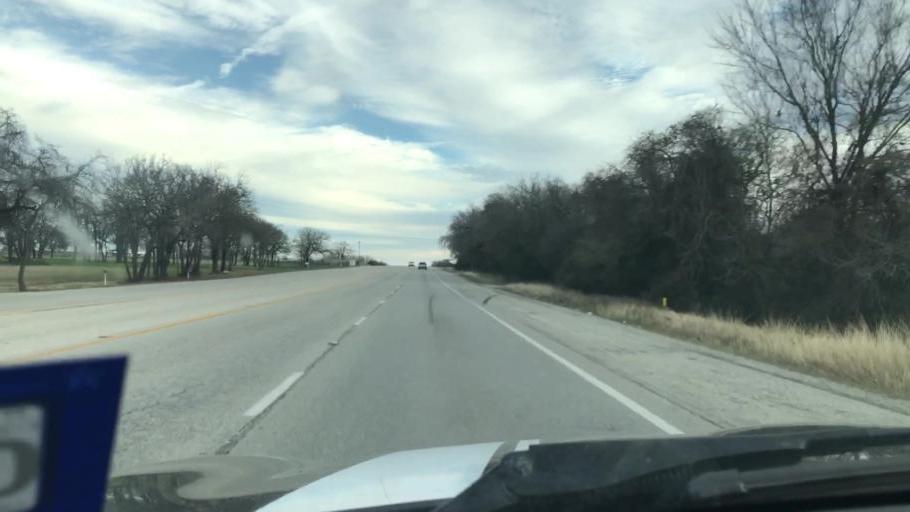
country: US
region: Texas
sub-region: Bastrop County
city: Camp Swift
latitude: 30.2909
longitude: -97.2537
